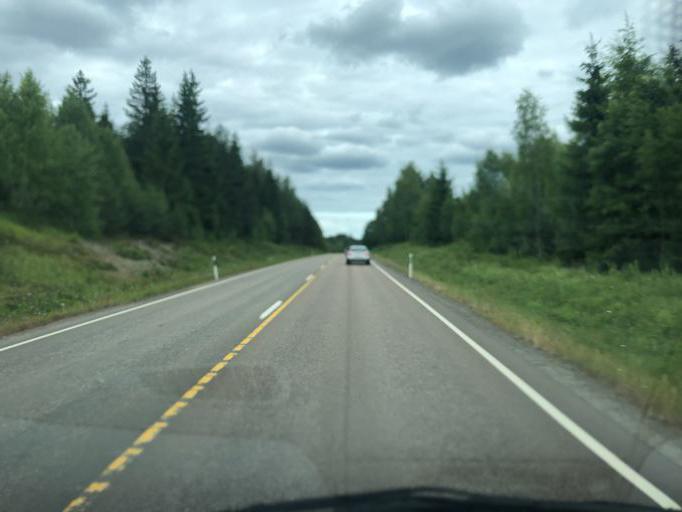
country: FI
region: Kymenlaakso
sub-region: Kouvola
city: Kouvola
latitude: 61.0535
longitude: 27.0343
